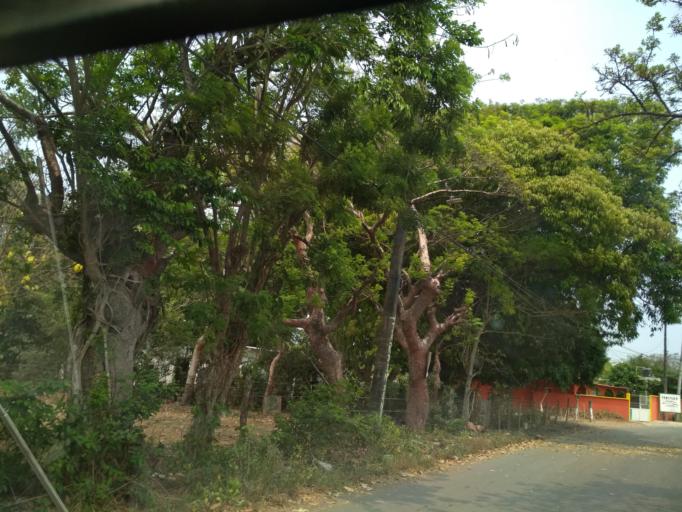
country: MX
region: Veracruz
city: El Tejar
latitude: 19.0693
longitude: -96.1548
